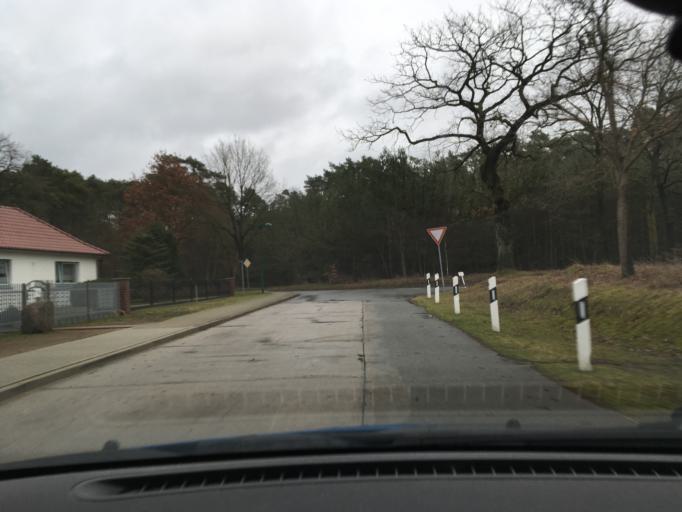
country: DE
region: Mecklenburg-Vorpommern
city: Nostorf
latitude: 53.4320
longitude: 10.6921
